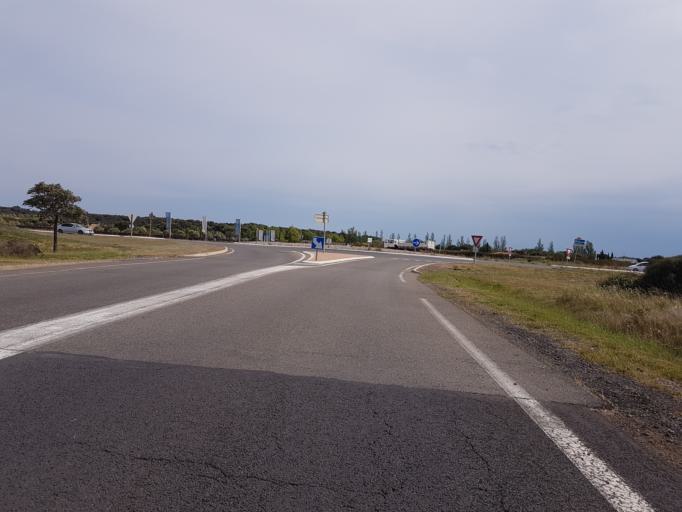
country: FR
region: Languedoc-Roussillon
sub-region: Departement de l'Herault
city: Portiragnes
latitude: 43.3149
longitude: 3.3605
